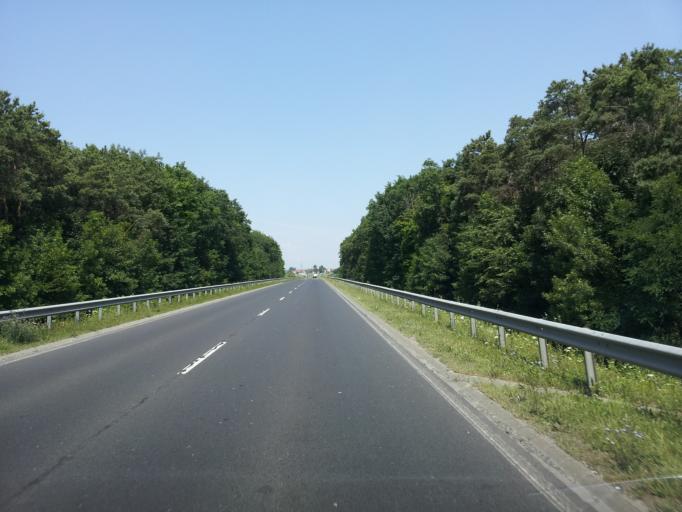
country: HU
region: Zala
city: Zalaegerszeg
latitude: 46.8491
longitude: 16.8635
